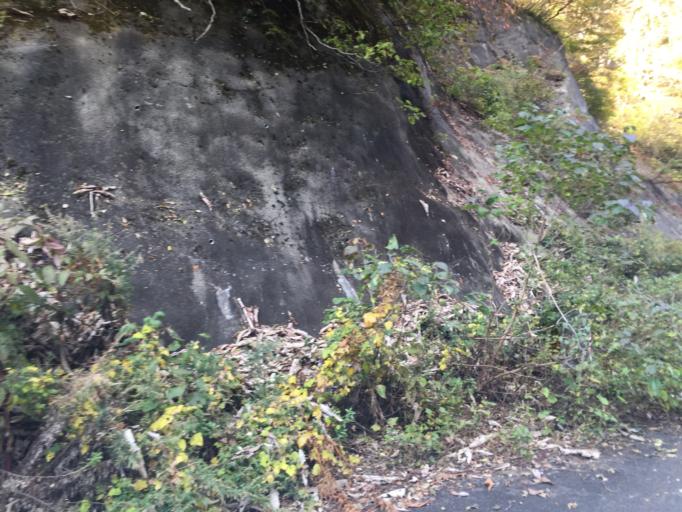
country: JP
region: Fukushima
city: Kitakata
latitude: 37.7473
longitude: 139.9283
